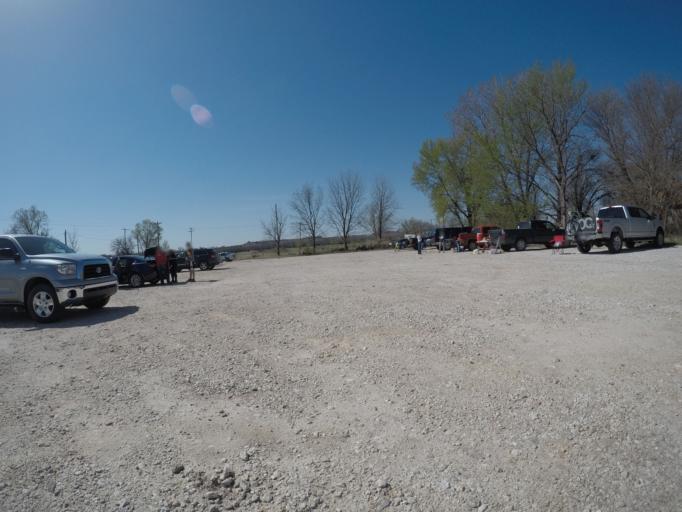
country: US
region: Kansas
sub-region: Pratt County
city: Pratt
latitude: 37.3790
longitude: -98.9156
